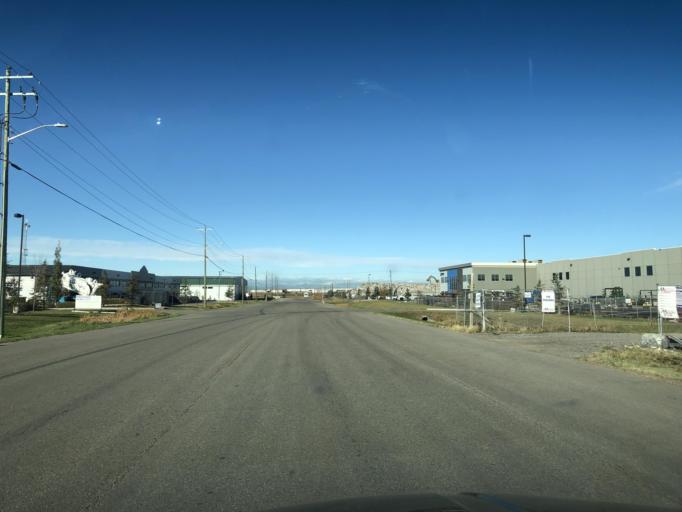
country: CA
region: Alberta
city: Chestermere
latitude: 50.9624
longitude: -113.9051
